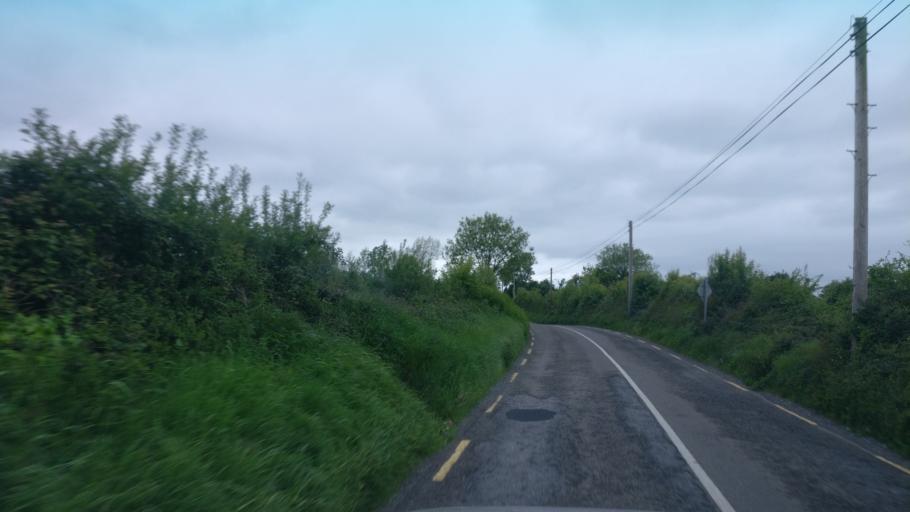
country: IE
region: Connaught
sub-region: County Galway
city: Portumna
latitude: 53.1048
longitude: -8.2582
